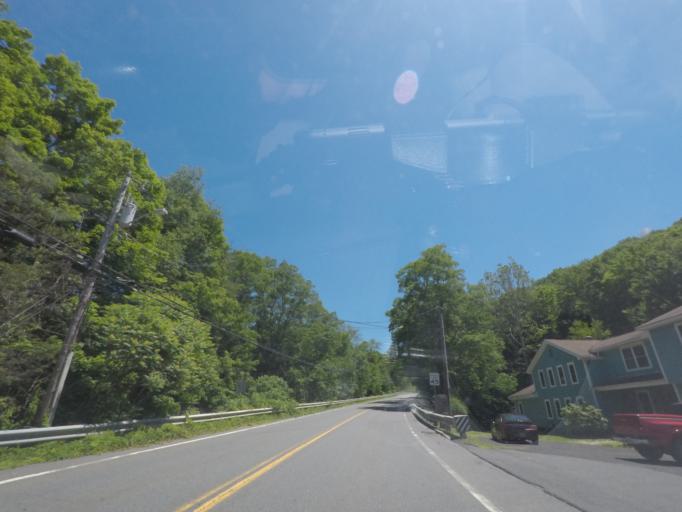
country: US
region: Massachusetts
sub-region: Berkshire County
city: Becket
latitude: 42.2757
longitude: -72.9727
